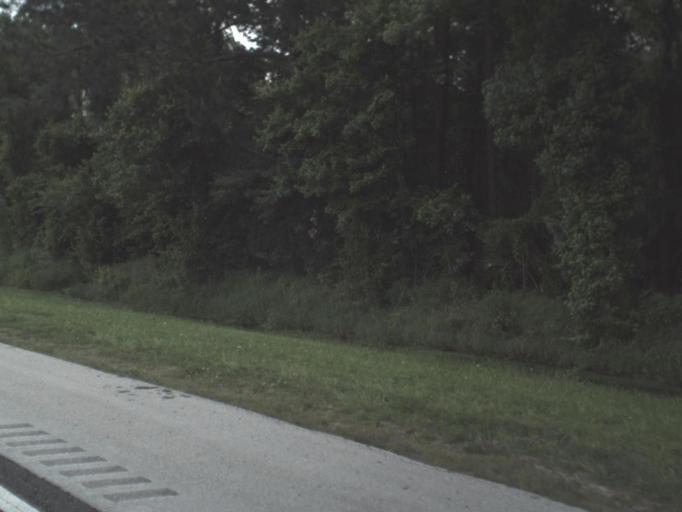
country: US
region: Florida
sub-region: Saint Johns County
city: Villano Beach
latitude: 29.9754
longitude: -81.4552
